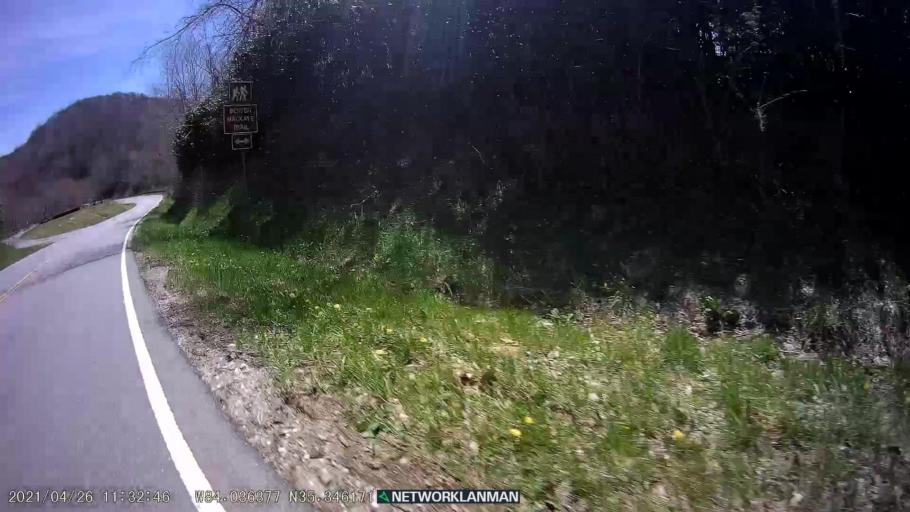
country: US
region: North Carolina
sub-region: Graham County
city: Robbinsville
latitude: 35.3459
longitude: -84.0362
